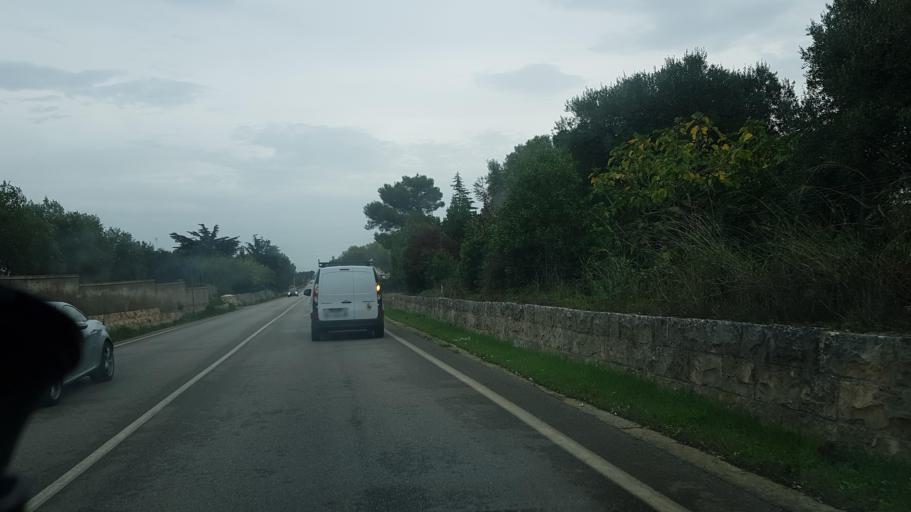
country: IT
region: Apulia
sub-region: Provincia di Brindisi
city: Ostuni
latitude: 40.7202
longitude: 17.6077
